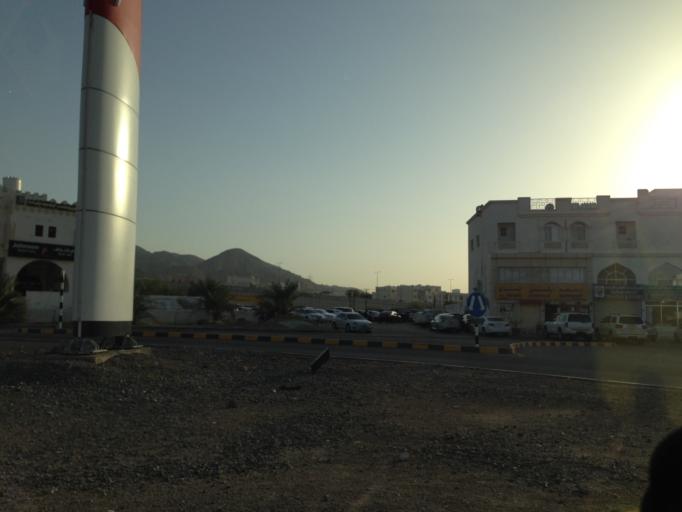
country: OM
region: Muhafazat Masqat
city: Bawshar
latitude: 23.5919
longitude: 58.4588
